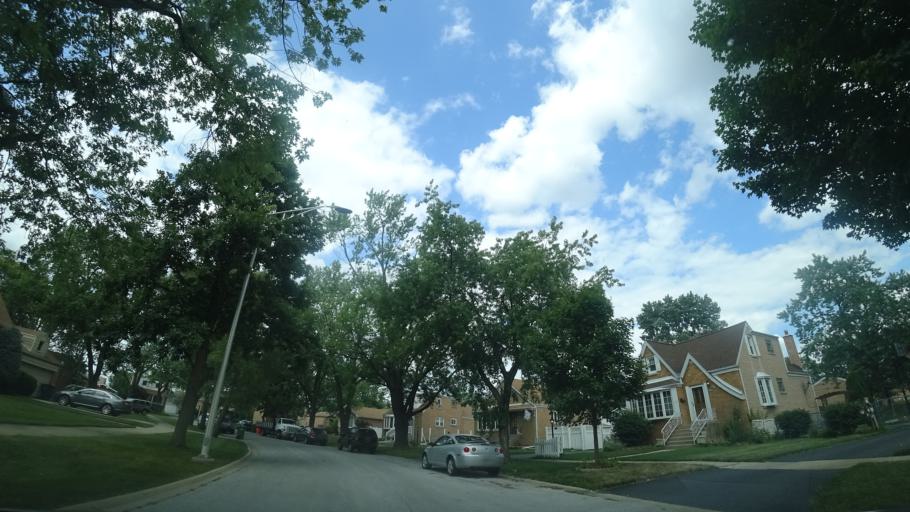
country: US
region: Illinois
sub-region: Cook County
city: Alsip
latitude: 41.6941
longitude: -87.7273
